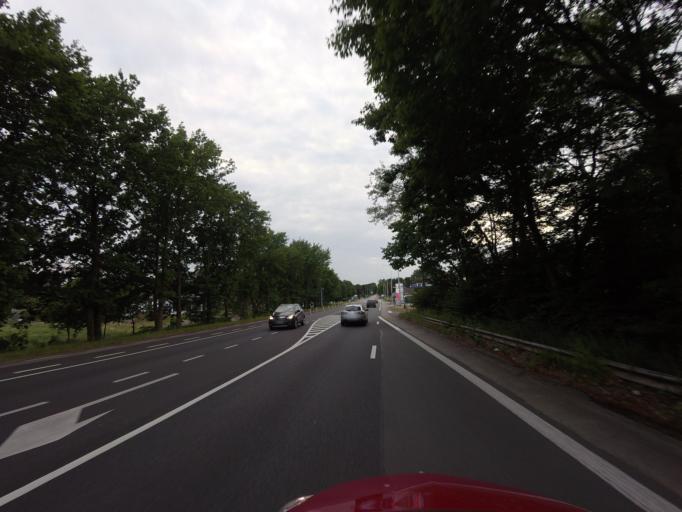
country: BE
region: Flanders
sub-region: Provincie Antwerpen
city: Lille
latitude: 51.2575
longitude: 4.8016
